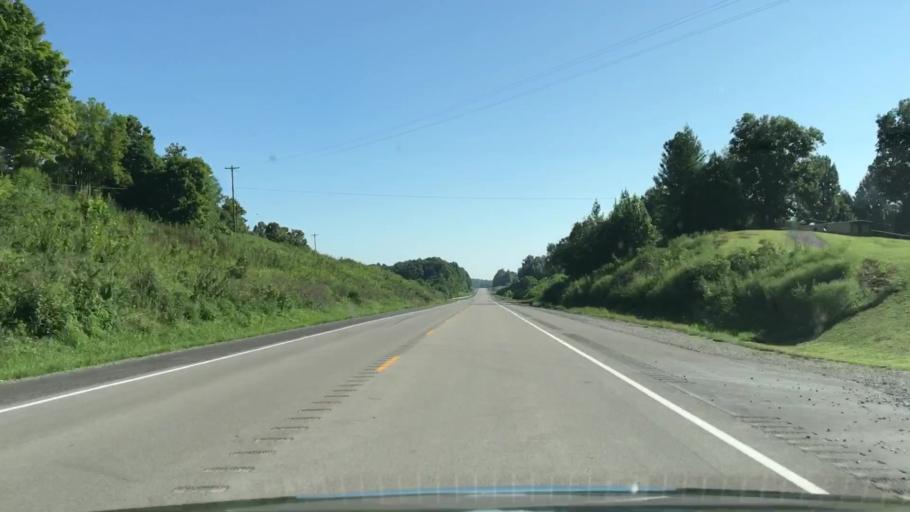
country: US
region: Tennessee
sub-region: Clay County
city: Celina
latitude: 36.6322
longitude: -85.3953
